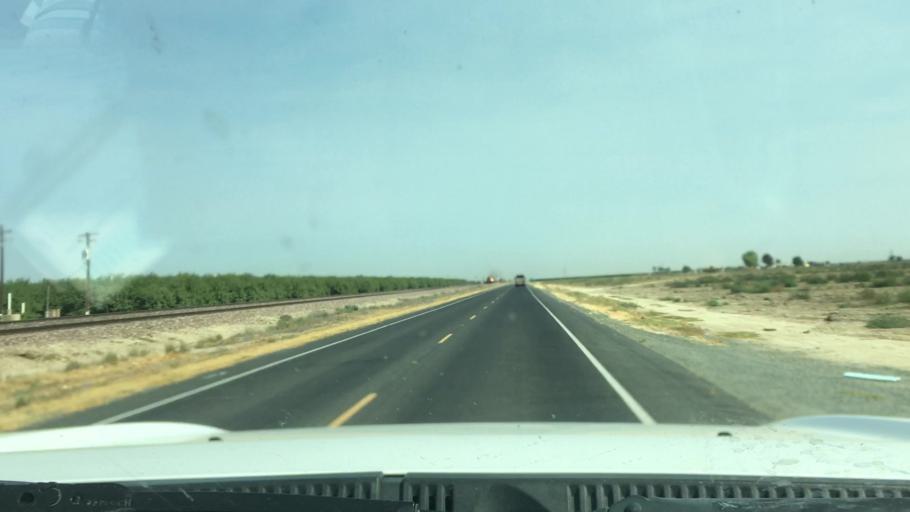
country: US
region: California
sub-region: Kern County
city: Delano
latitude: 35.7679
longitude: -119.3474
